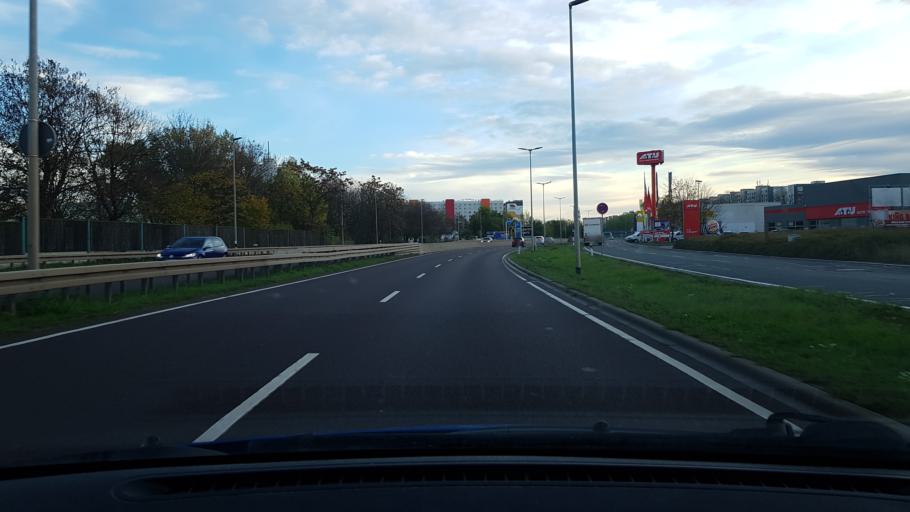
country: DE
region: Saxony-Anhalt
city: Barleben
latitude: 52.1775
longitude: 11.6284
